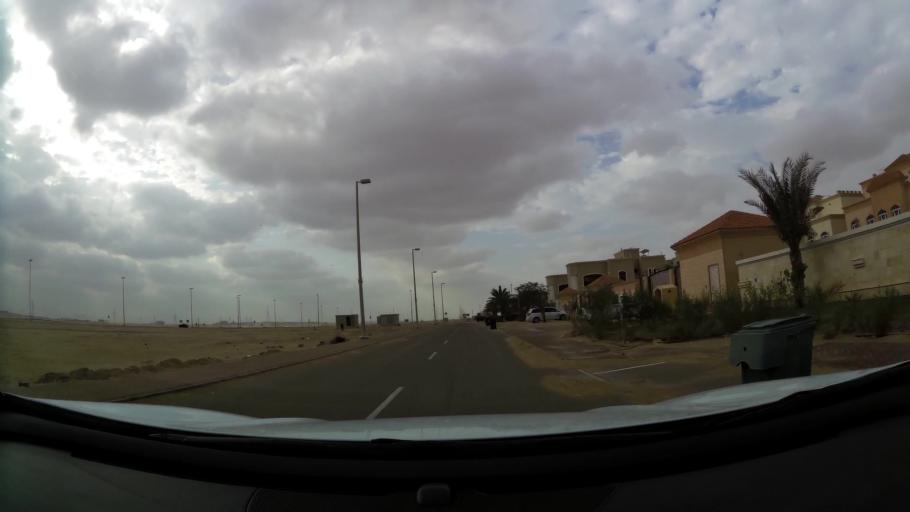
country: AE
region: Abu Dhabi
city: Abu Dhabi
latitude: 24.3444
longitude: 54.6137
